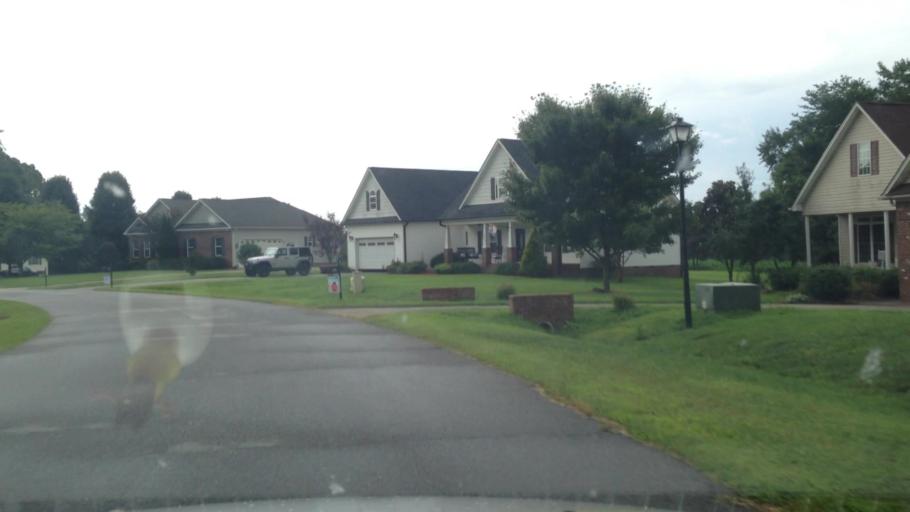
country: US
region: North Carolina
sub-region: Rockingham County
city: Reidsville
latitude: 36.2666
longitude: -79.7160
